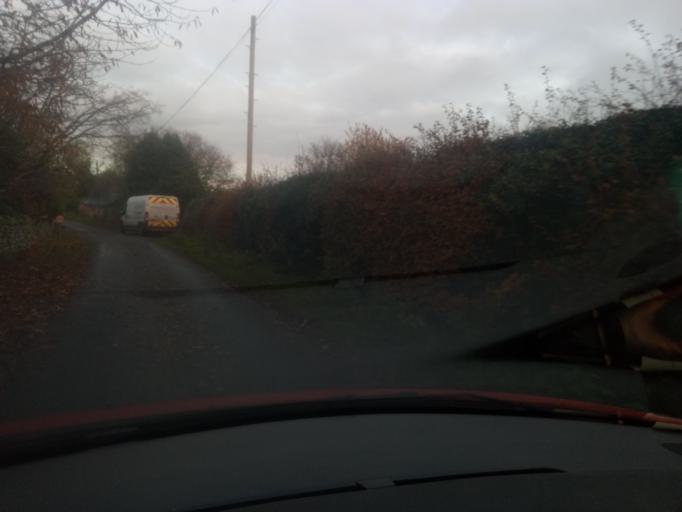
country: GB
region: Scotland
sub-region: The Scottish Borders
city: Jedburgh
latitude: 55.4861
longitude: -2.6053
